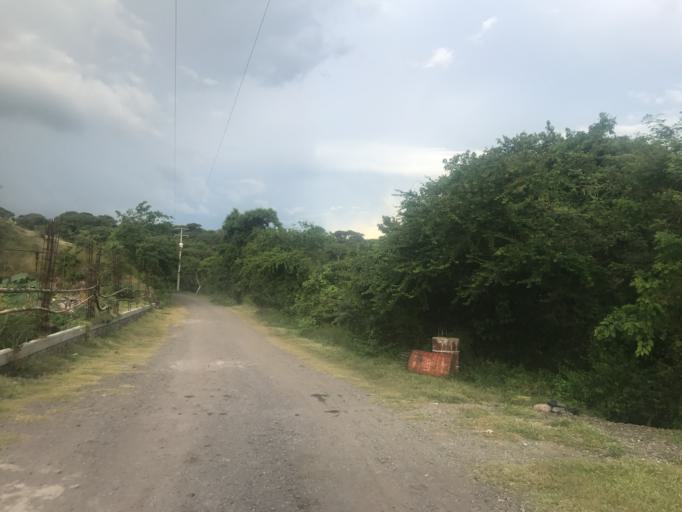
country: MX
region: Morelos
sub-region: Axochiapan
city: Quebrantadero
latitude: 18.5171
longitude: -98.8089
